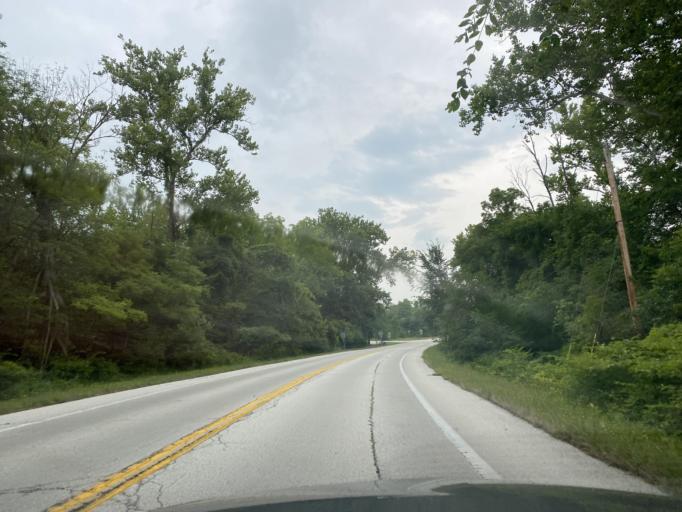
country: US
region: Ohio
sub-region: Summit County
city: Fairlawn
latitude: 41.1801
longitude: -81.5833
